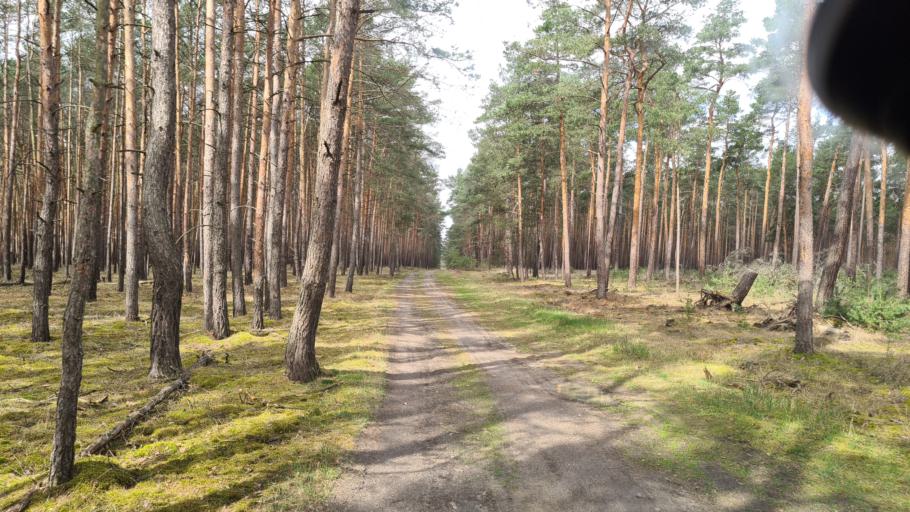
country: DE
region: Brandenburg
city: Trobitz
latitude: 51.6569
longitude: 13.4432
